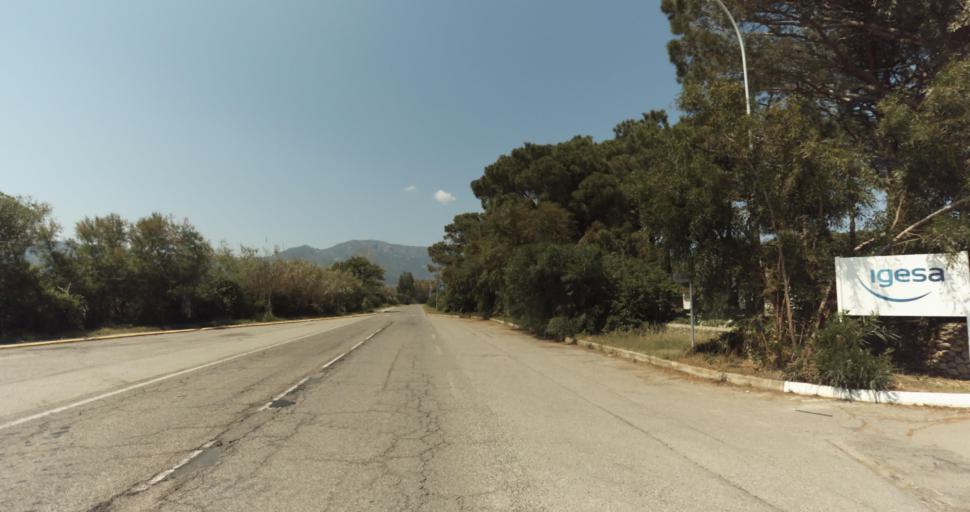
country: FR
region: Corsica
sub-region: Departement de la Haute-Corse
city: Biguglia
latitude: 42.6432
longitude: 9.4568
